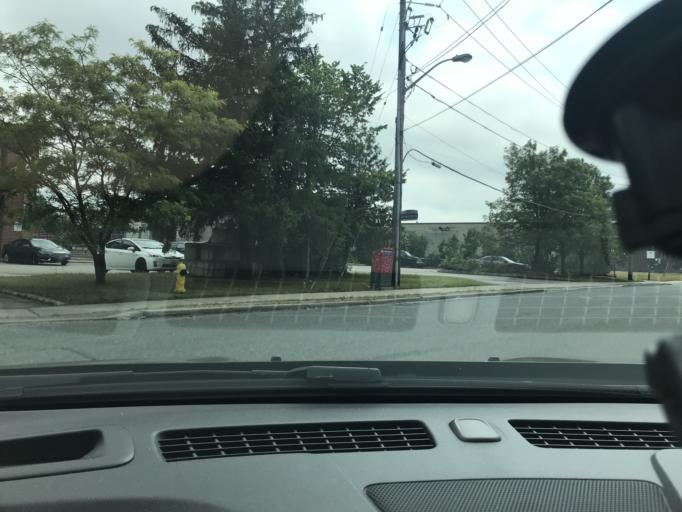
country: CA
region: Ontario
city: Concord
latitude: 43.7581
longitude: -79.4810
